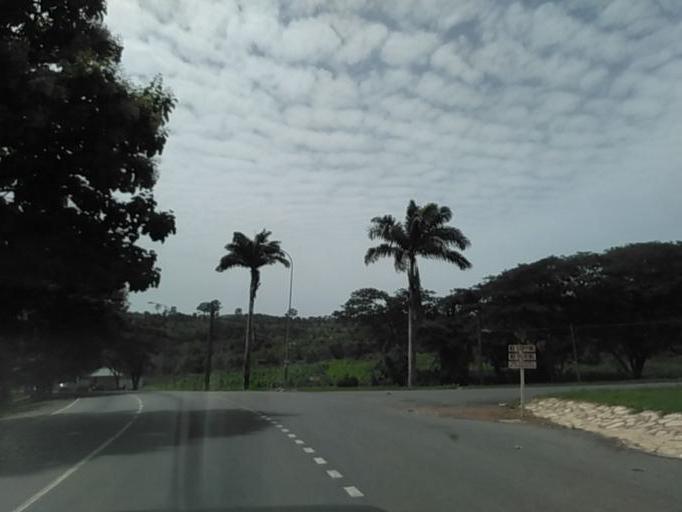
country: GH
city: Akropong
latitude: 6.2642
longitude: 0.0591
